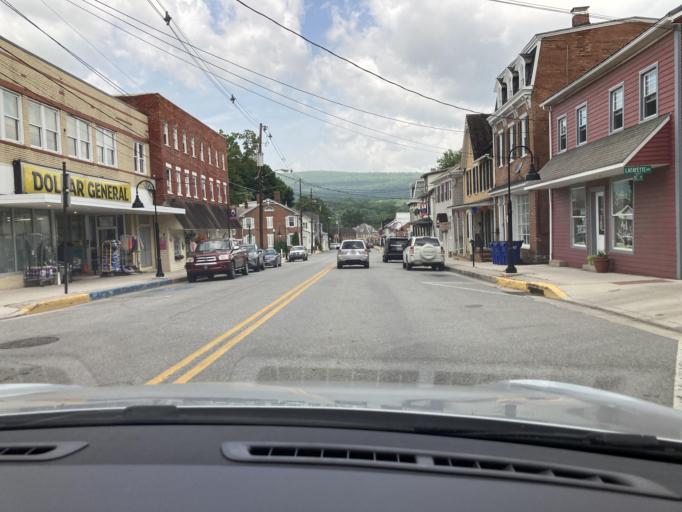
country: US
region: Pennsylvania
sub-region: Bedford County
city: Bedford
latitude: 40.0190
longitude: -78.5046
